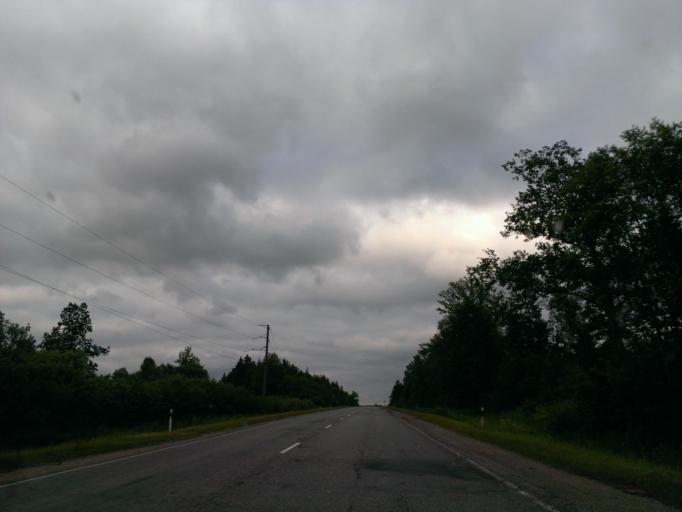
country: LV
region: Saldus Rajons
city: Saldus
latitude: 56.6706
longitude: 22.3957
